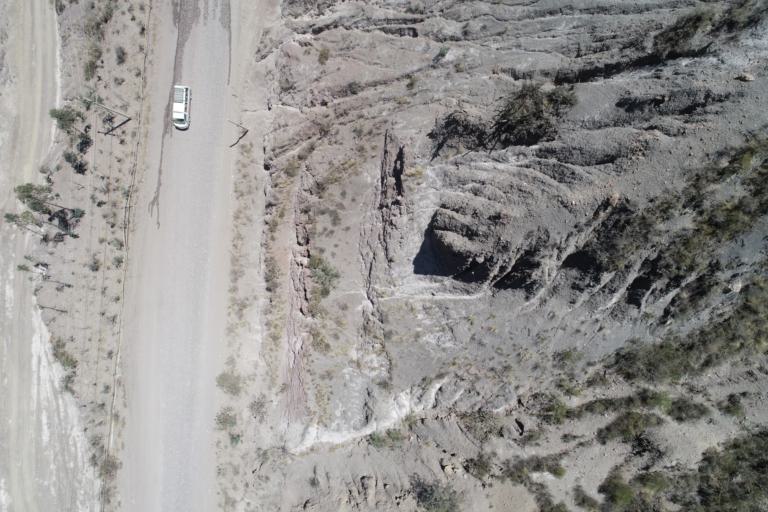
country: BO
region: La Paz
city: La Paz
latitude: -16.6147
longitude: -68.0590
